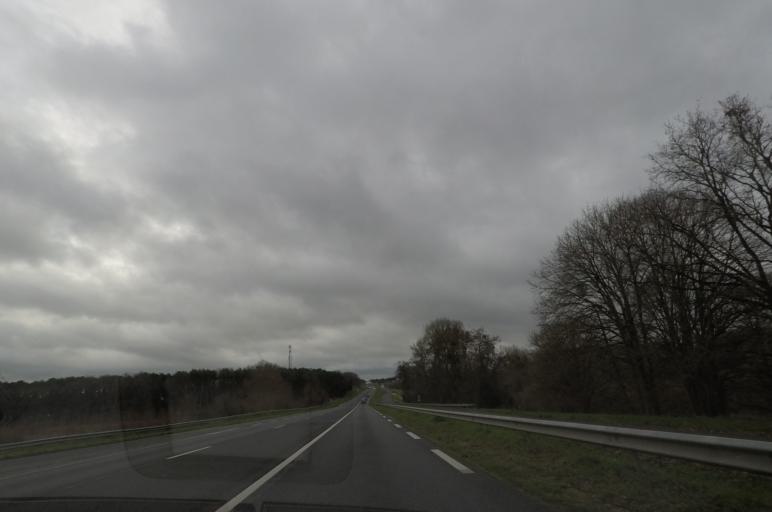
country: FR
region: Centre
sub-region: Departement du Loir-et-Cher
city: Saint-Sulpice-de-Pommeray
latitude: 47.6547
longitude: 1.2712
